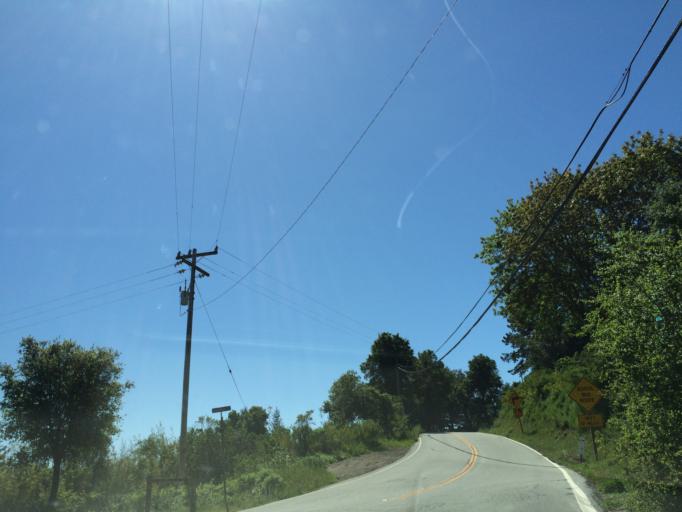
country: US
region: California
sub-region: Santa Clara County
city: Lexington Hills
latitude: 37.1658
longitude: -122.0160
